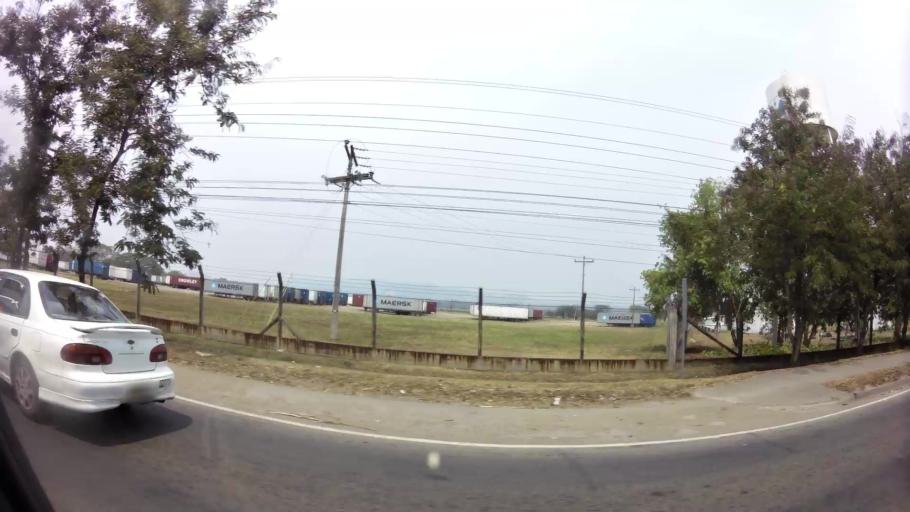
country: HN
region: Cortes
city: Villanueva
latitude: 15.3261
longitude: -87.9926
